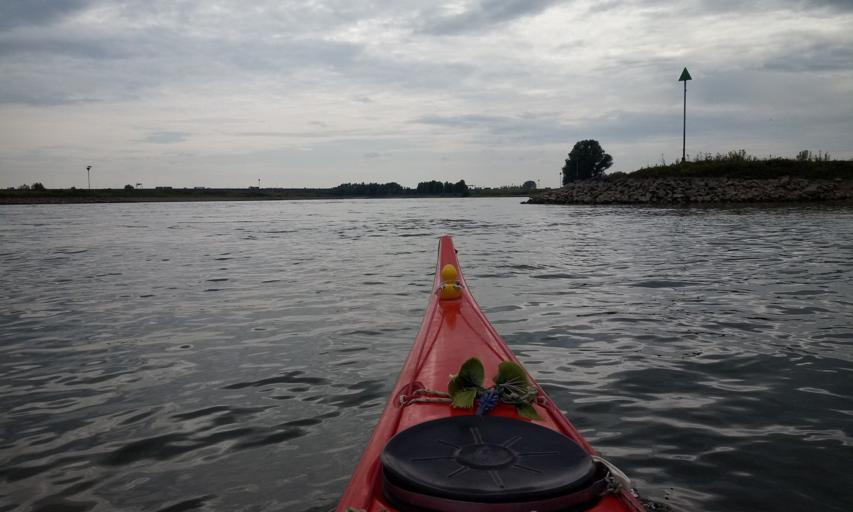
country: NL
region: Overijssel
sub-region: Gemeente Deventer
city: Deventer
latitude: 52.2410
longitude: 6.1620
